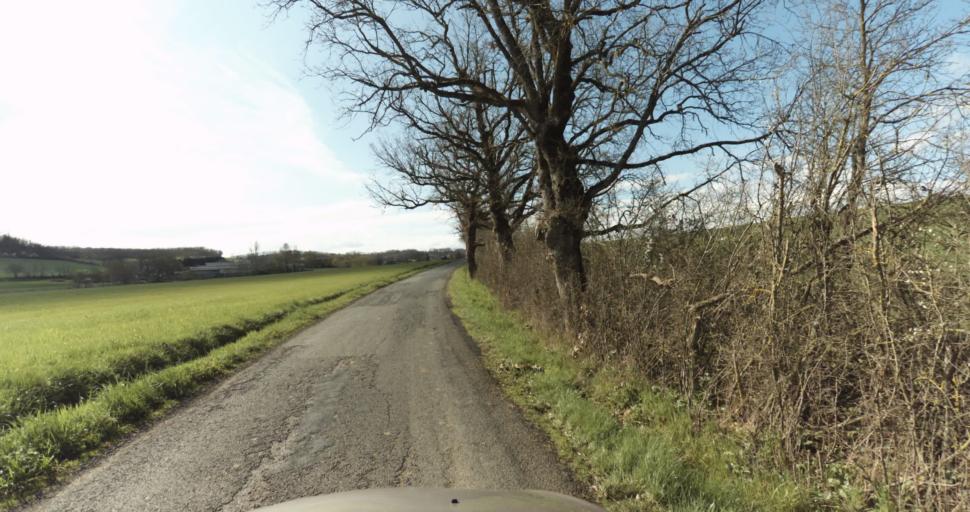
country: FR
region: Midi-Pyrenees
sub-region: Departement du Tarn
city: Puygouzon
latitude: 43.8801
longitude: 2.1822
